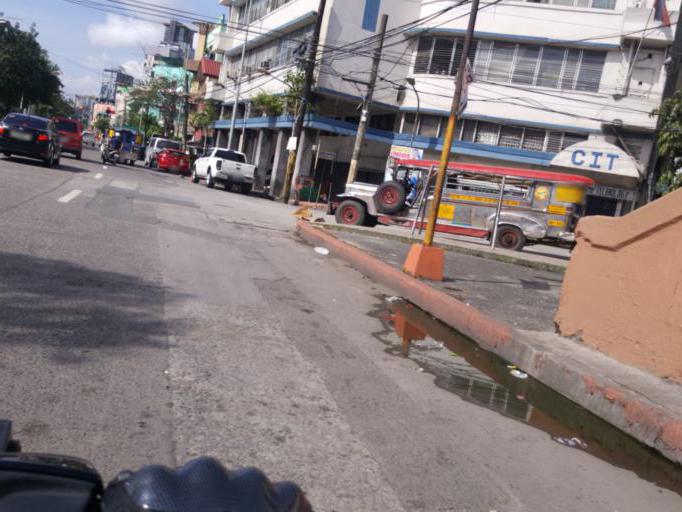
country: PH
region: Metro Manila
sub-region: City of Manila
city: Manila
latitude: 14.6068
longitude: 120.9859
